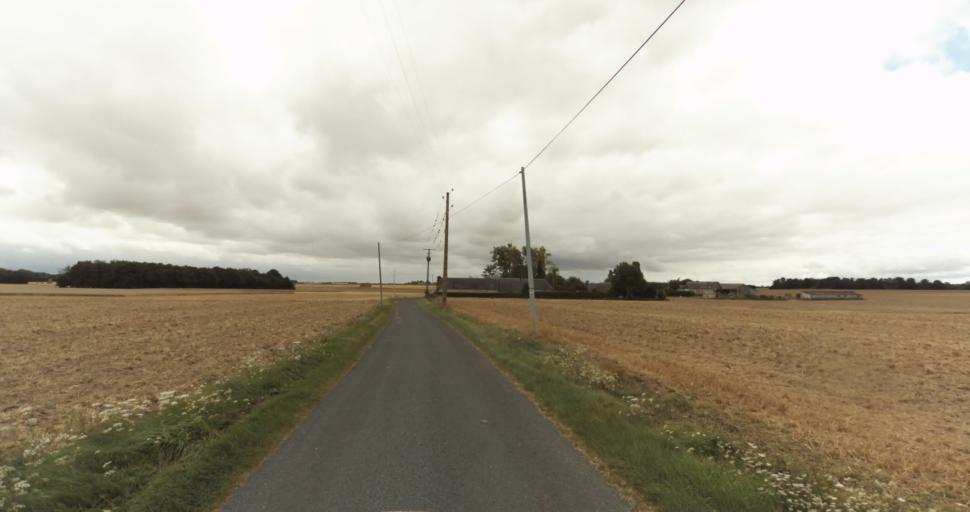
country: FR
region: Haute-Normandie
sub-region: Departement de l'Eure
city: Evreux
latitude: 48.9056
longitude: 1.2078
